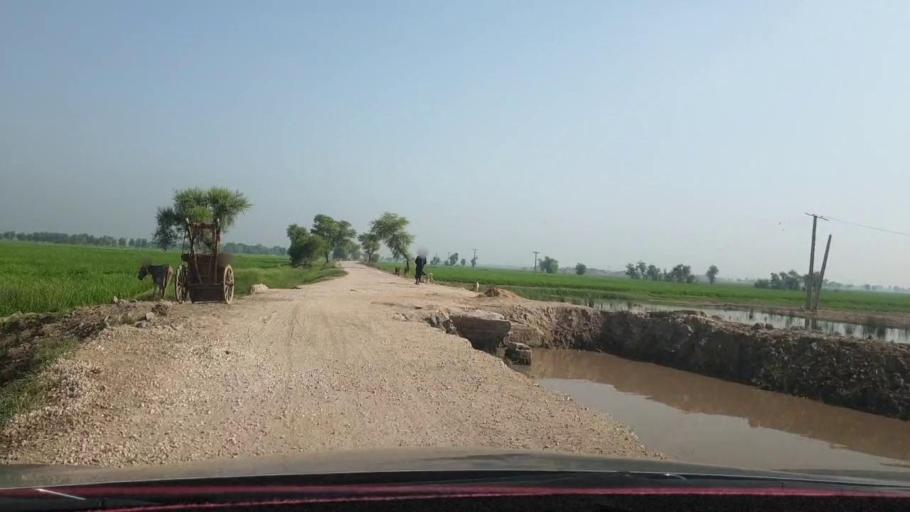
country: PK
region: Sindh
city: Nasirabad
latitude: 27.4864
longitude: 67.9260
